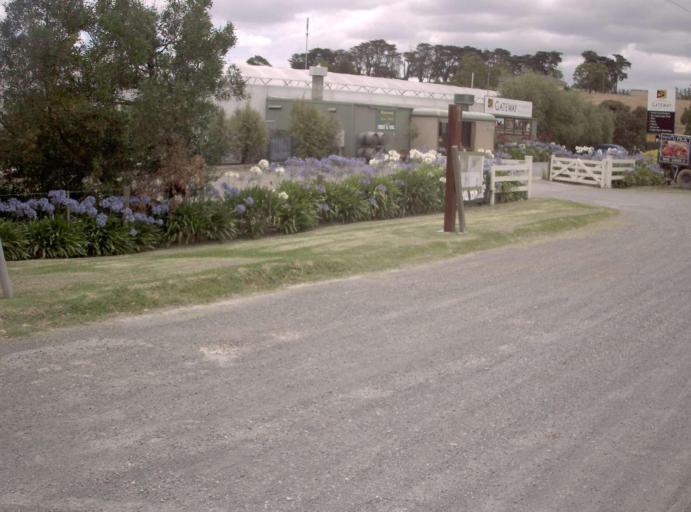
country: AU
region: Victoria
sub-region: Yarra Ranges
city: Lilydale
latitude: -37.7239
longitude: 145.3787
